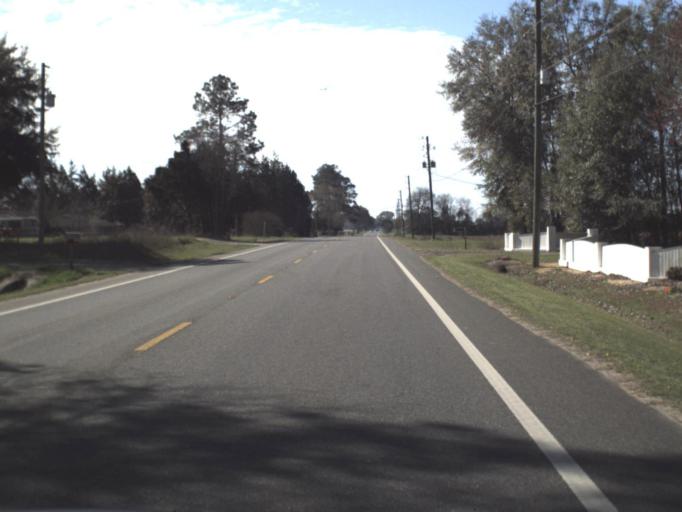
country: US
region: Florida
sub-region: Jackson County
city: Malone
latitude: 30.8594
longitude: -85.1635
